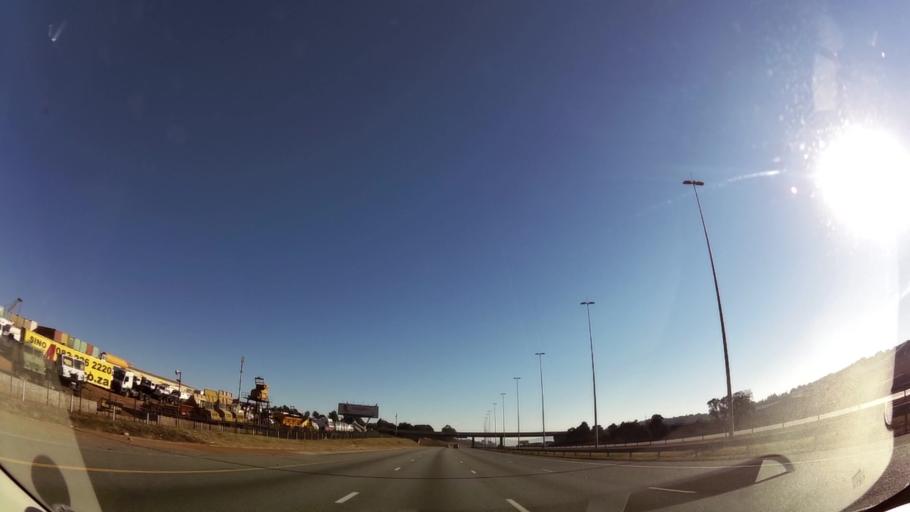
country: ZA
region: Gauteng
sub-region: City of Tshwane Metropolitan Municipality
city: Centurion
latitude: -25.9061
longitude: 28.2558
